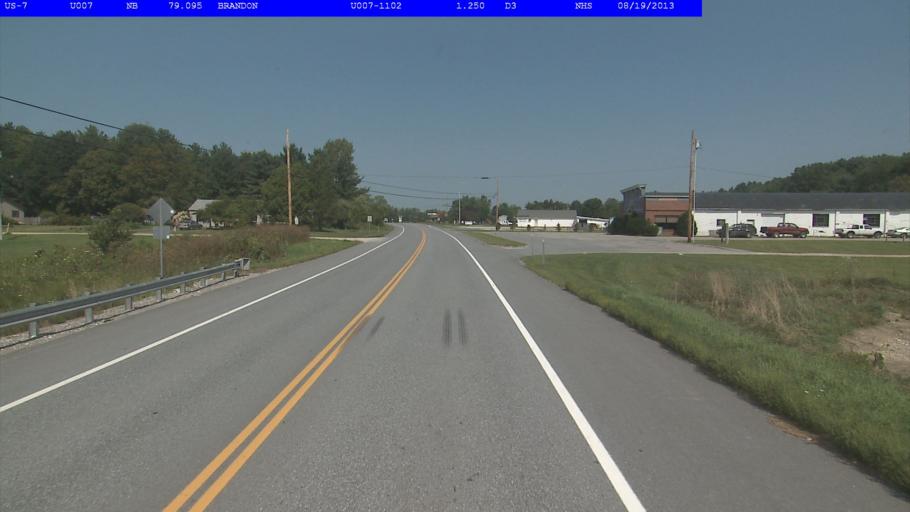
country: US
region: Vermont
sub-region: Rutland County
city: Brandon
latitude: 43.7722
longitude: -73.0520
